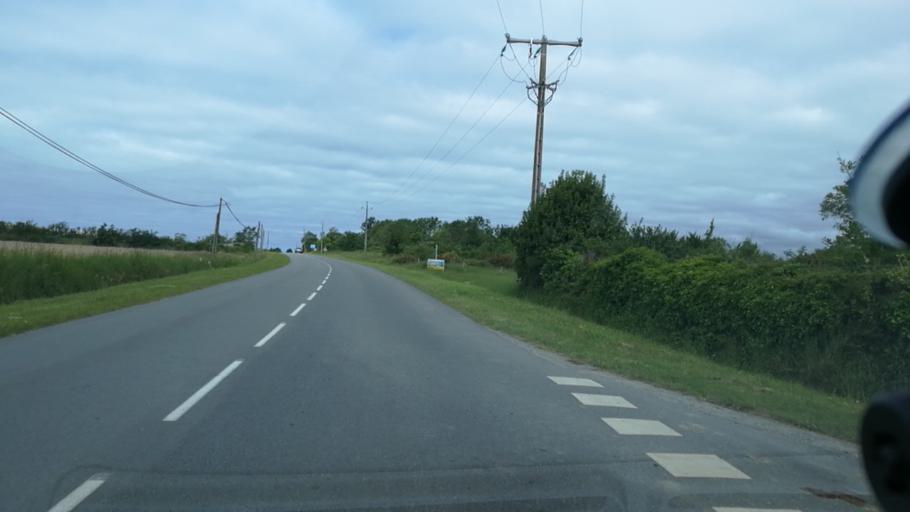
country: FR
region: Brittany
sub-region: Departement du Morbihan
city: Penestin
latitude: 47.4554
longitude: -2.4663
